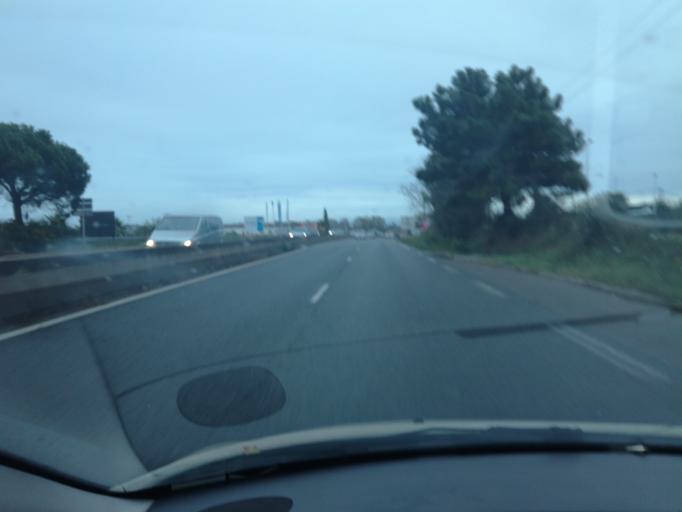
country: FR
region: Provence-Alpes-Cote d'Azur
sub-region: Departement du Var
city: Puget-sur-Argens
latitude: 43.4419
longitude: 6.7044
